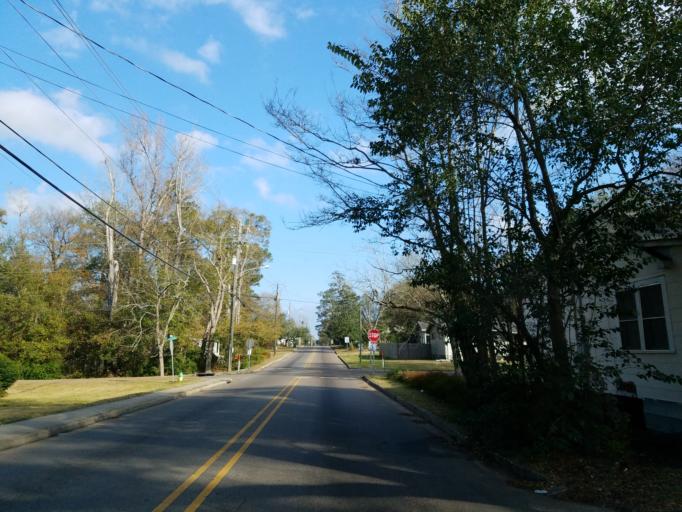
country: US
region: Mississippi
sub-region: Forrest County
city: Hattiesburg
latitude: 31.3357
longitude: -89.3199
